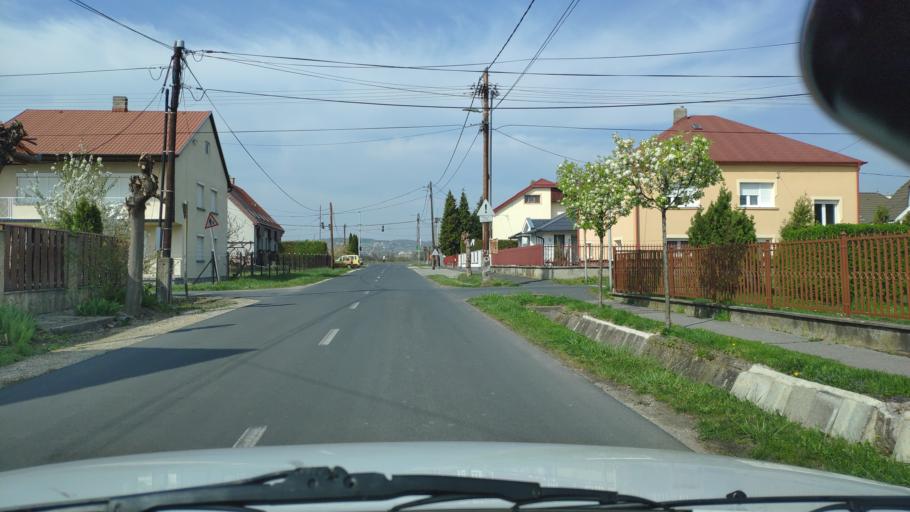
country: HU
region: Zala
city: Keszthely
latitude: 46.7713
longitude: 17.2631
